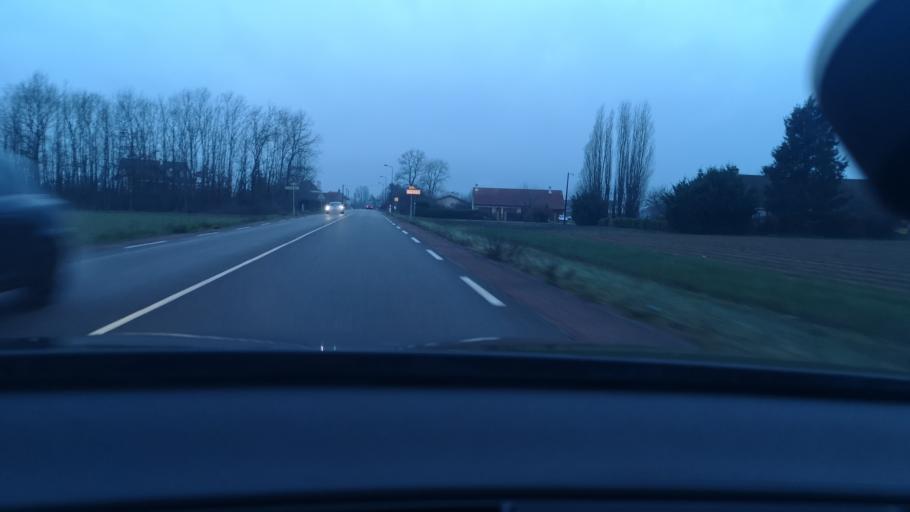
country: FR
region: Bourgogne
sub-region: Departement de Saone-et-Loire
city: Verdun-sur-le-Doubs
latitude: 47.0055
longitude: 5.0017
